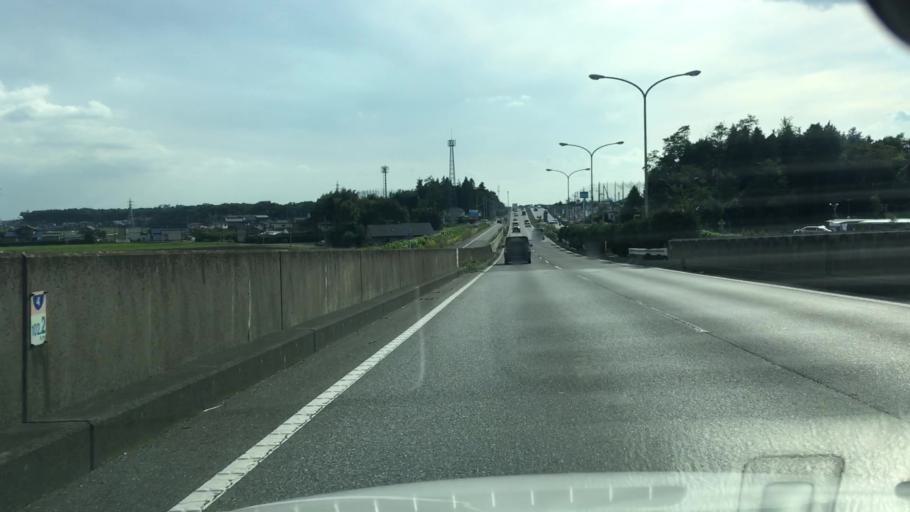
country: JP
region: Tochigi
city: Utsunomiya-shi
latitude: 36.5358
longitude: 139.9307
